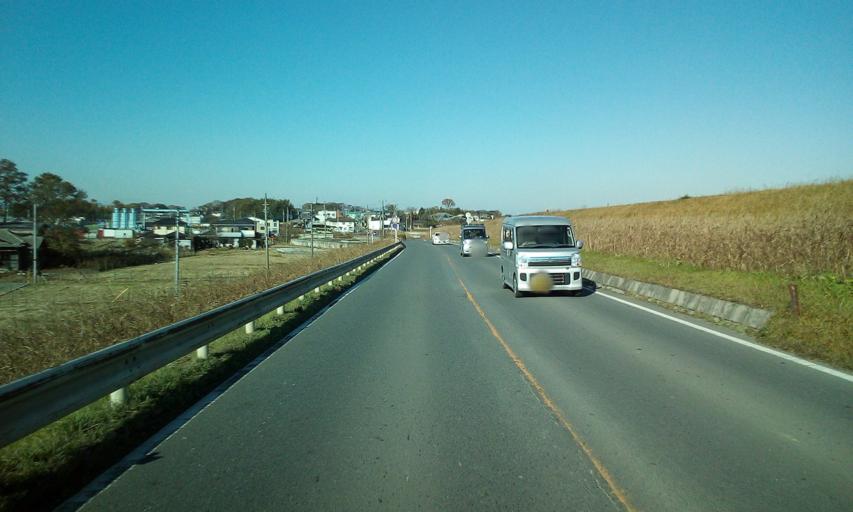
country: JP
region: Chiba
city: Noda
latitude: 35.9427
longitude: 139.8414
